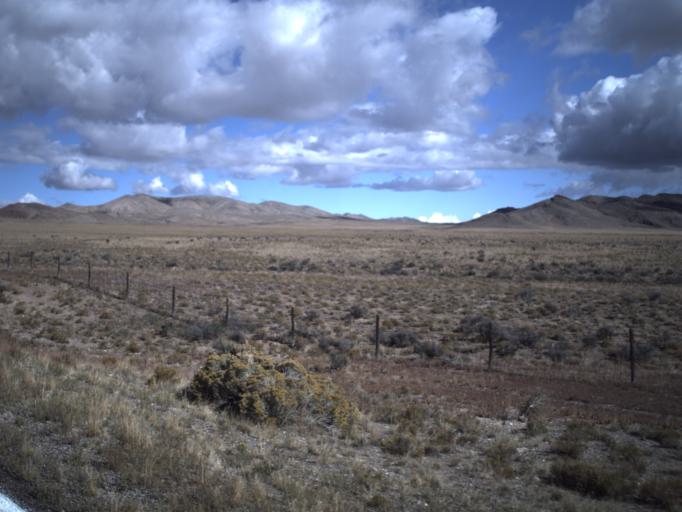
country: US
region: Utah
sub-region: Beaver County
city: Milford
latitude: 38.5919
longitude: -113.8210
